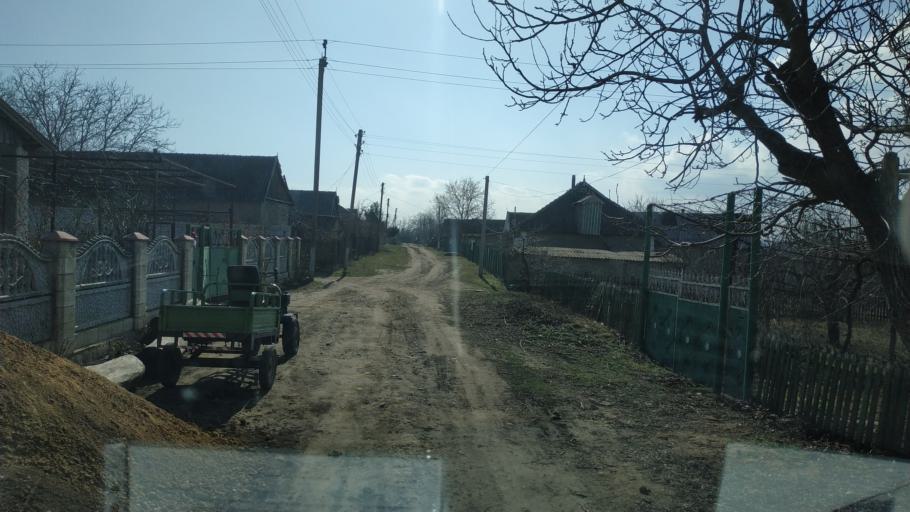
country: MD
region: Basarabeasca
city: Basarabeasca
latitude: 46.5752
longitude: 29.1187
